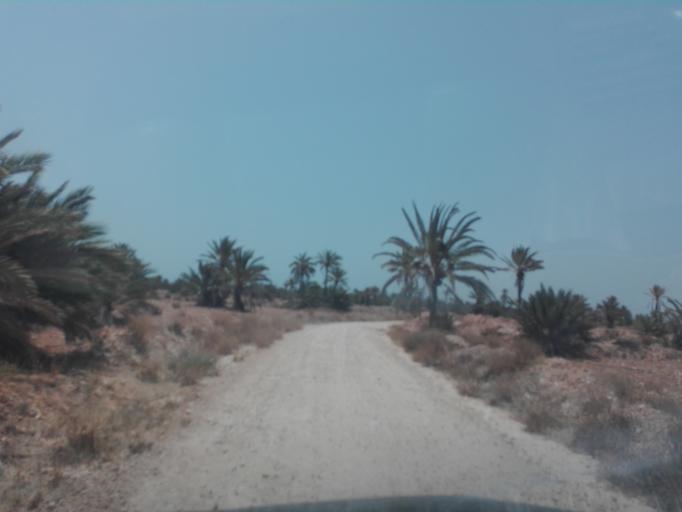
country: TN
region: Safaqis
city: Al Qarmadah
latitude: 34.6623
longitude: 11.0959
